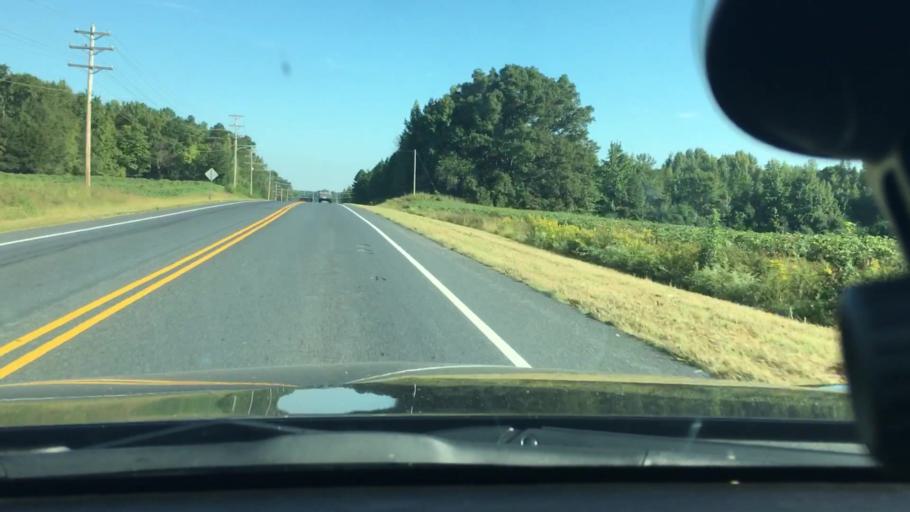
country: US
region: North Carolina
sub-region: Stanly County
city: Albemarle
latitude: 35.3687
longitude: -80.1700
